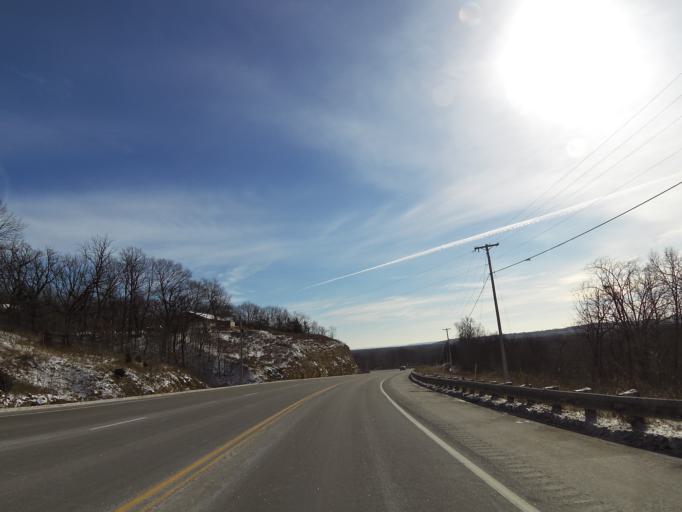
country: US
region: Wisconsin
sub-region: Pierce County
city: Prescott
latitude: 44.7542
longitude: -92.8256
